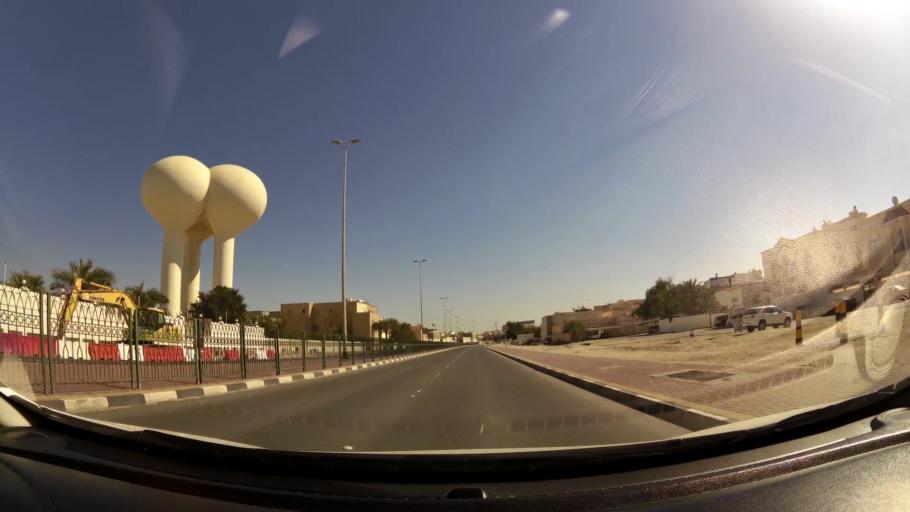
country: BH
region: Muharraq
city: Al Hadd
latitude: 26.2495
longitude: 50.6516
